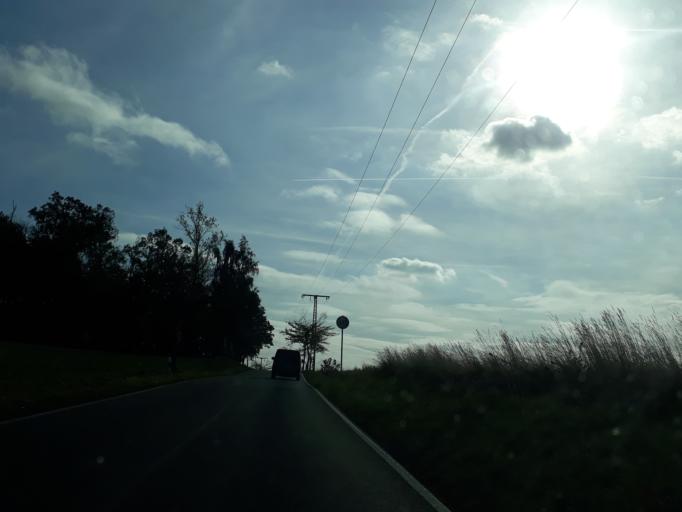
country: DE
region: Saxony
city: Klipphausen
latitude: 51.0769
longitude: 13.5788
